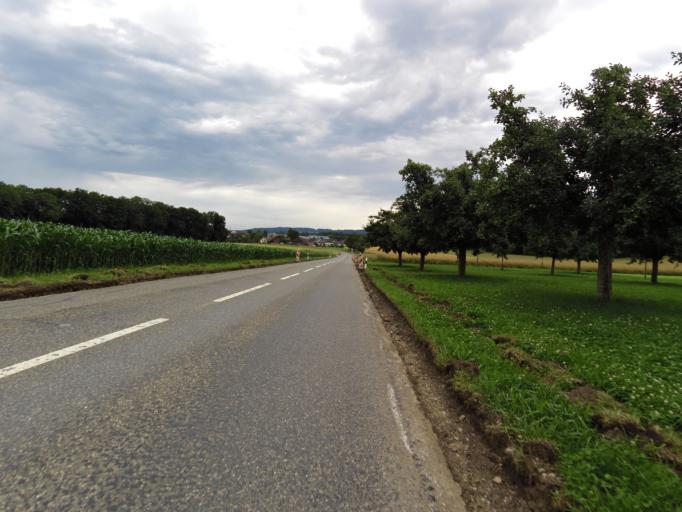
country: CH
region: Thurgau
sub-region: Frauenfeld District
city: Gachnang
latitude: 47.5631
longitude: 8.8617
